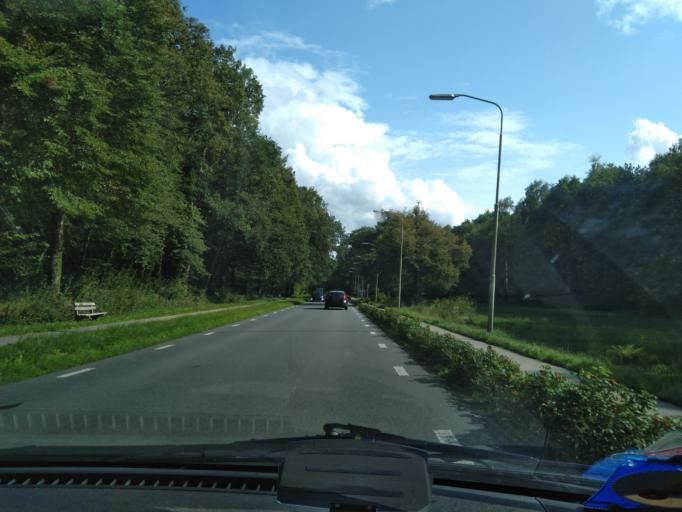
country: NL
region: Groningen
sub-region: Gemeente Haren
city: Haren
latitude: 53.1630
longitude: 6.5561
